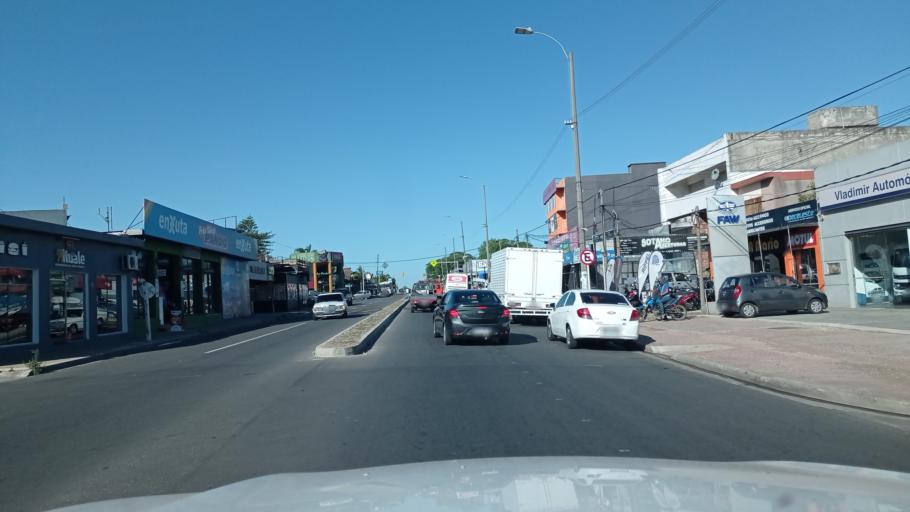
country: UY
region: Canelones
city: Pando
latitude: -34.7245
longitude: -55.9599
